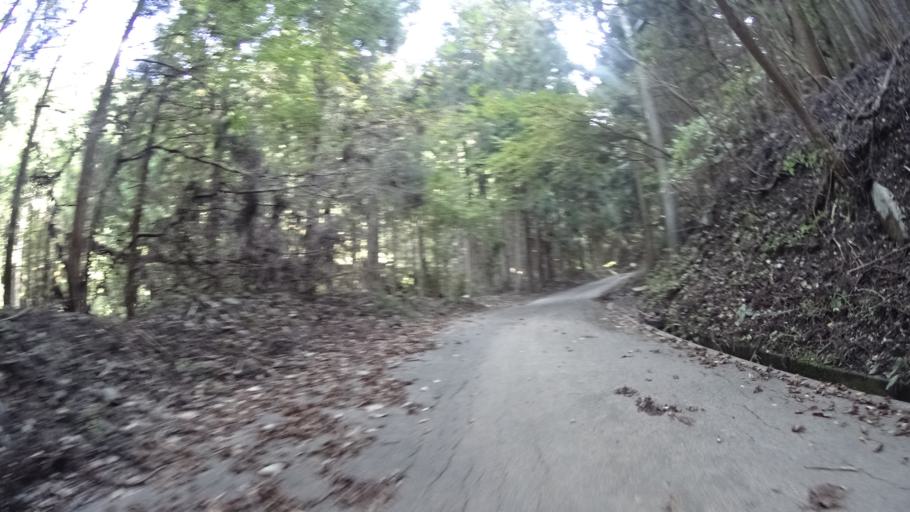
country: JP
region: Yamanashi
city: Otsuki
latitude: 35.5781
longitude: 138.9798
